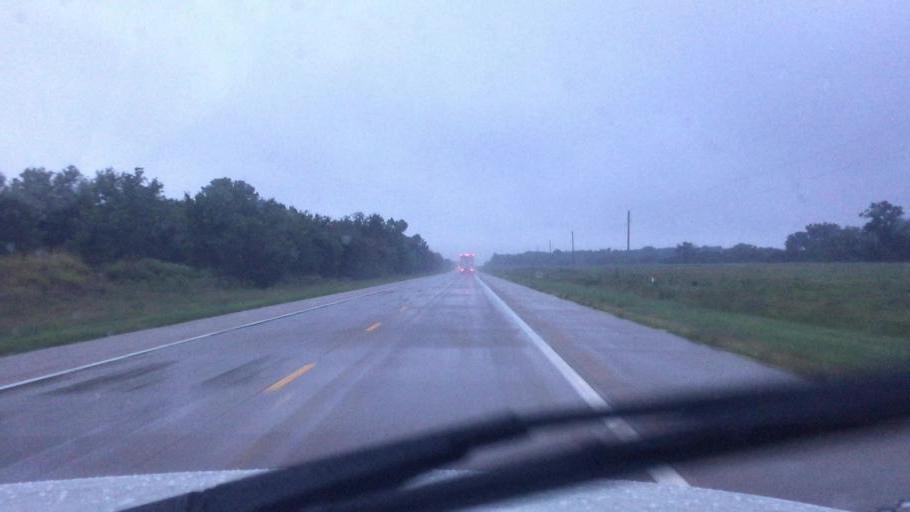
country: US
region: Kansas
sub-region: Neosho County
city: Chanute
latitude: 37.5553
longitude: -95.4709
